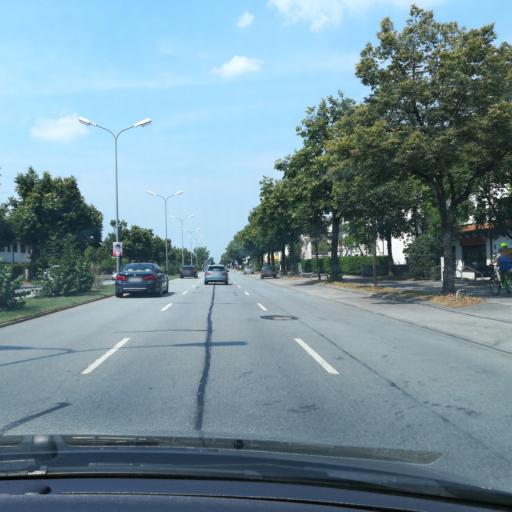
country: DE
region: Bavaria
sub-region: Upper Bavaria
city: Neuried
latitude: 48.1176
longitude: 11.5026
